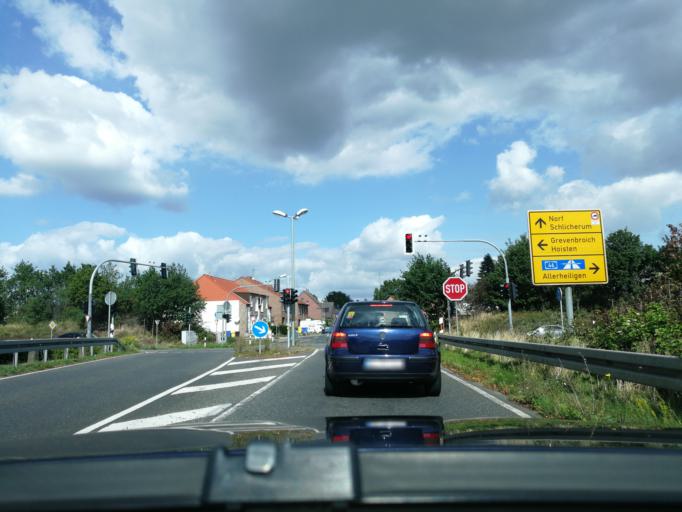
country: DE
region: North Rhine-Westphalia
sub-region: Regierungsbezirk Dusseldorf
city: Neuss
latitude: 51.1393
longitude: 6.7221
